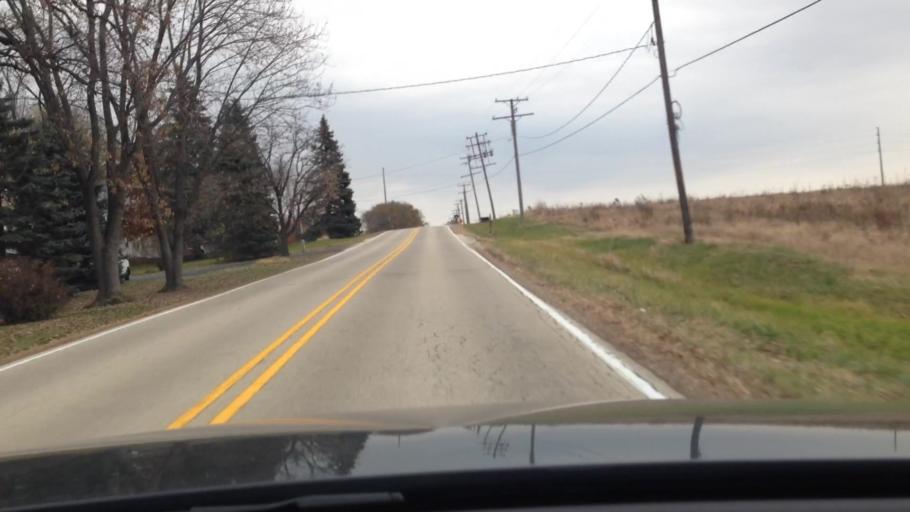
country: US
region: Illinois
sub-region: McHenry County
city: Woodstock
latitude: 42.2767
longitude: -88.4571
